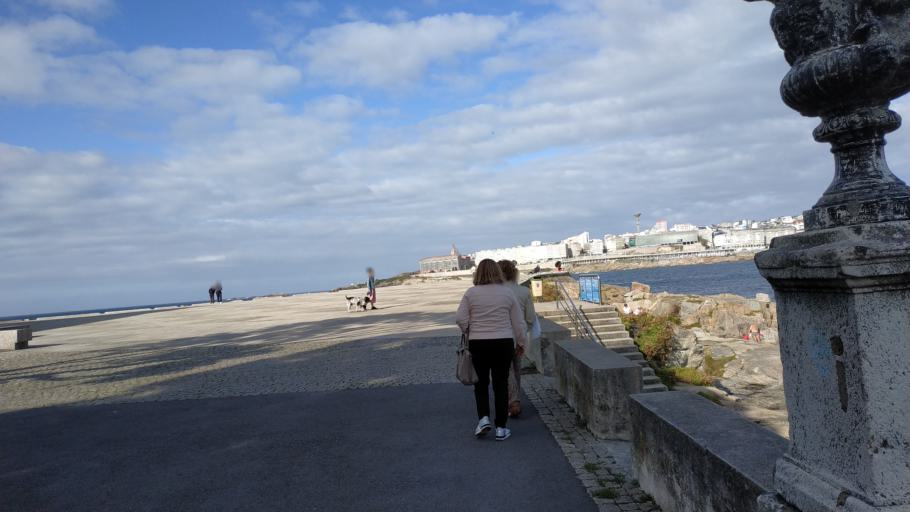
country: ES
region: Galicia
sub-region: Provincia da Coruna
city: A Coruna
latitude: 43.3702
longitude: -8.4145
